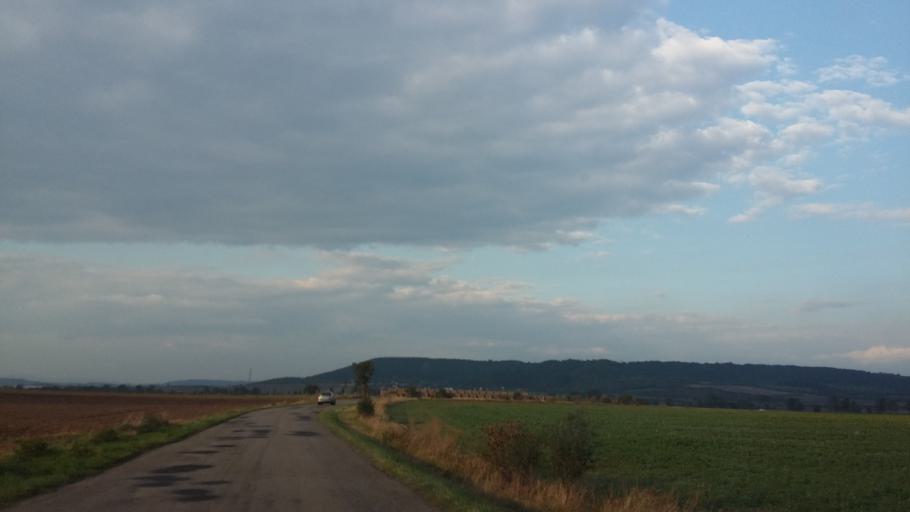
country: CZ
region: Central Bohemia
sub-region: Okres Mlada Boleslav
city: Mlada Boleslav
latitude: 50.3592
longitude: 14.8955
